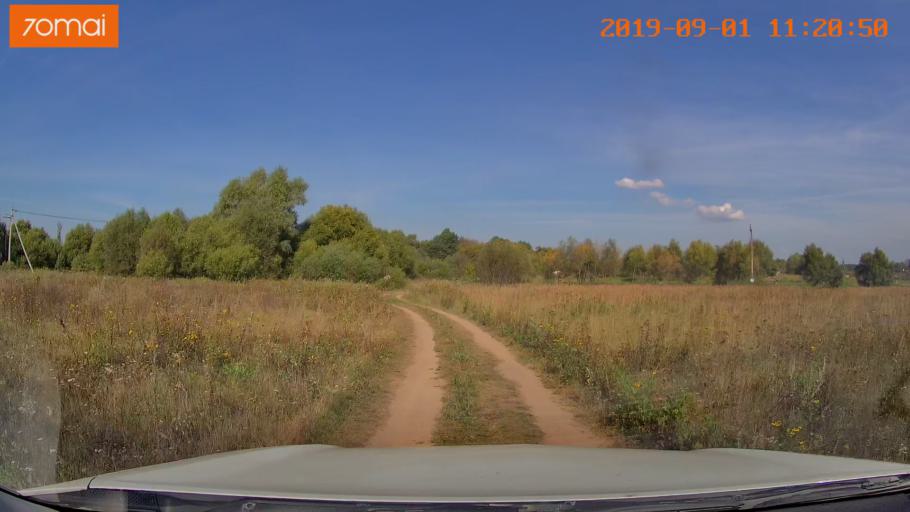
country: RU
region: Kaluga
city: Detchino
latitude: 54.8301
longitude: 36.3604
